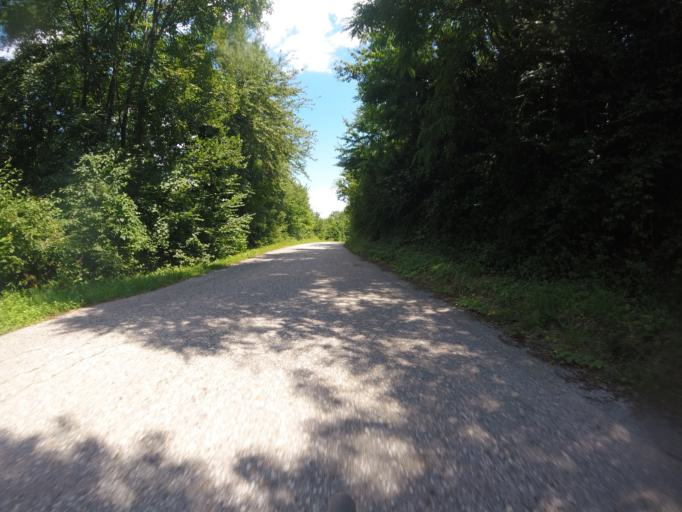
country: HR
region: Karlovacka
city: Ozalj
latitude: 45.6762
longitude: 15.4565
